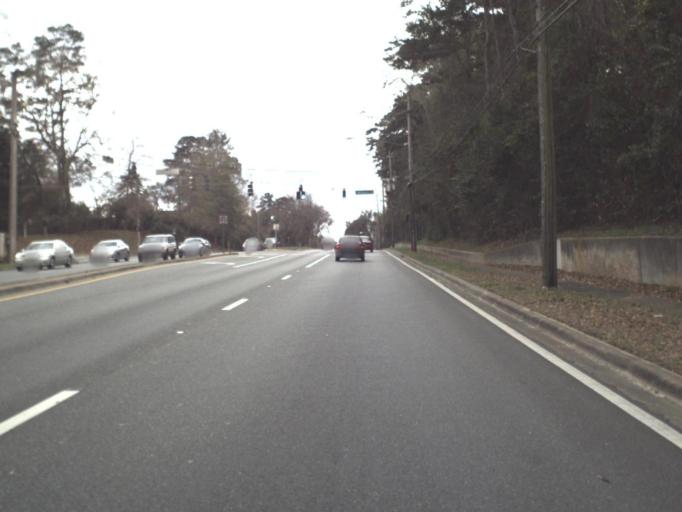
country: US
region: Florida
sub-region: Leon County
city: Tallahassee
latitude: 30.4870
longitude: -84.2563
